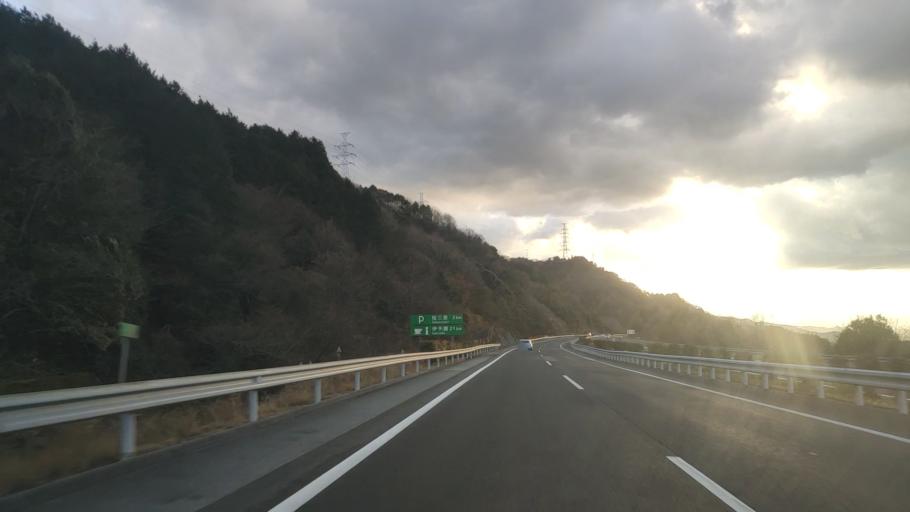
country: JP
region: Ehime
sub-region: Shikoku-chuo Shi
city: Matsuyama
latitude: 33.8148
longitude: 132.9565
